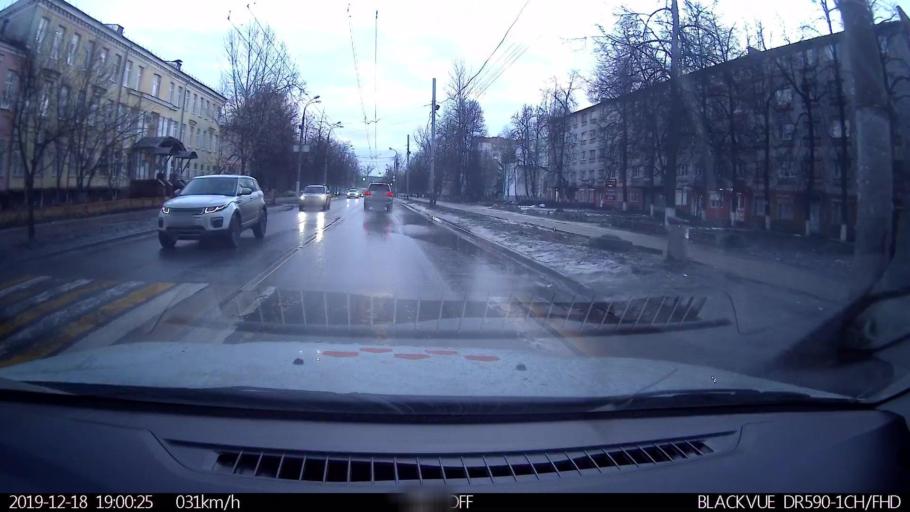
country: RU
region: Nizjnij Novgorod
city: Gorbatovka
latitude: 56.3294
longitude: 43.8504
